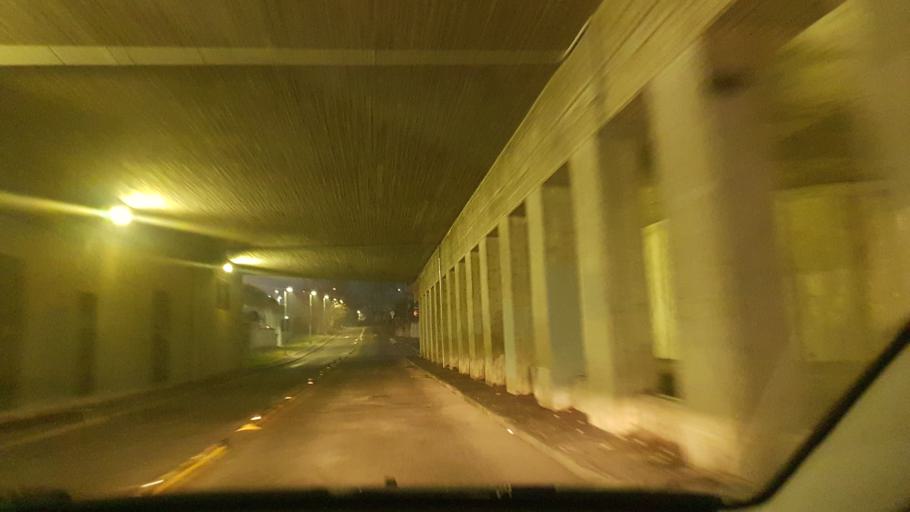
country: IT
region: Emilia-Romagna
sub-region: Provincia di Bologna
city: Bologna
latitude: 44.5134
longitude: 11.3286
